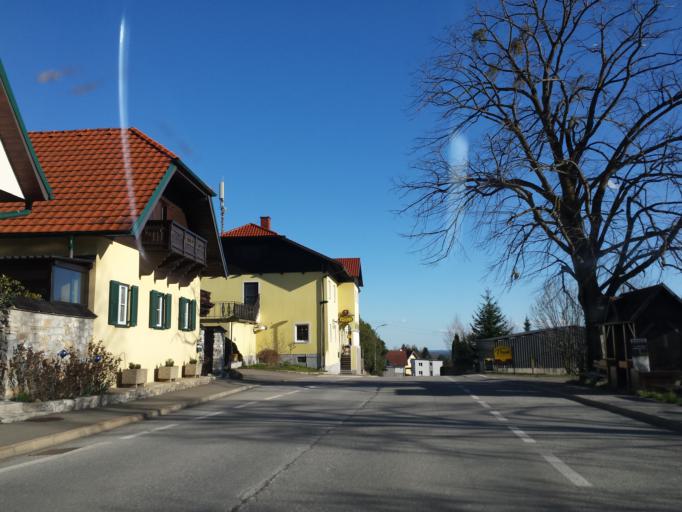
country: AT
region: Styria
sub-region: Politischer Bezirk Graz-Umgebung
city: Sankt Radegund bei Graz
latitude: 47.1611
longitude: 15.4901
